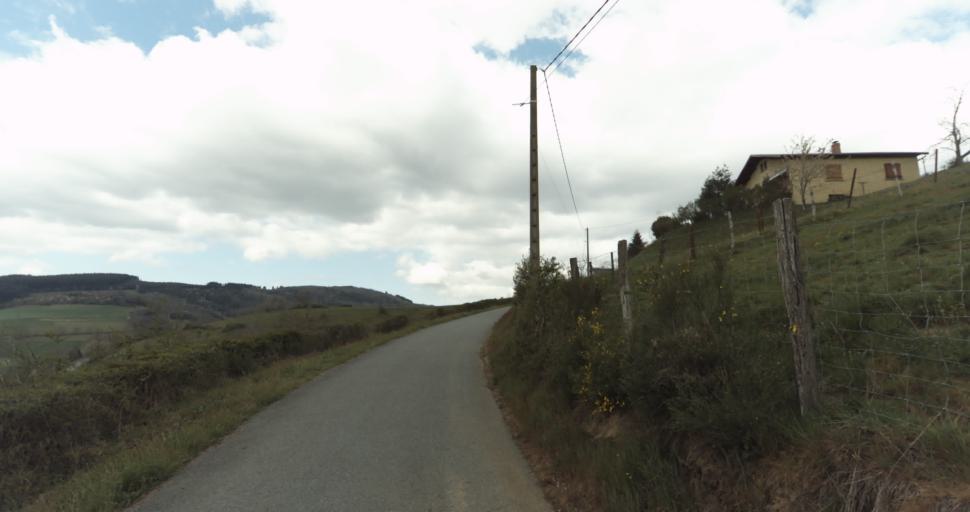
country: FR
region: Rhone-Alpes
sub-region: Departement du Rhone
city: Tarare
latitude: 45.9136
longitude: 4.4353
